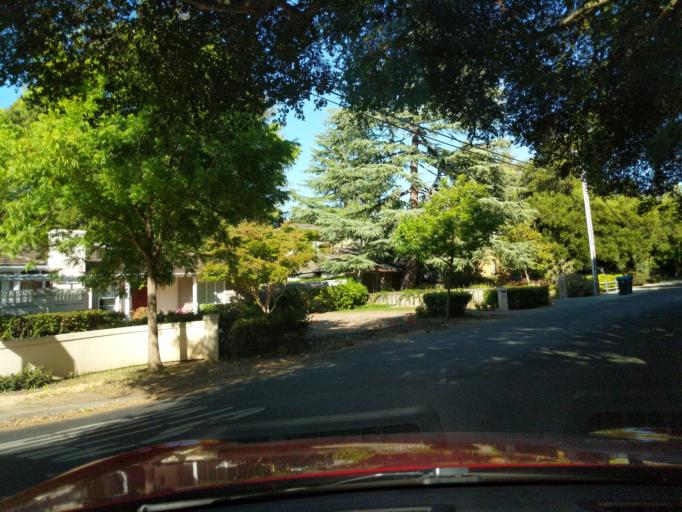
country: US
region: California
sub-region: San Mateo County
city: Menlo Park
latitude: 37.4419
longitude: -122.1842
